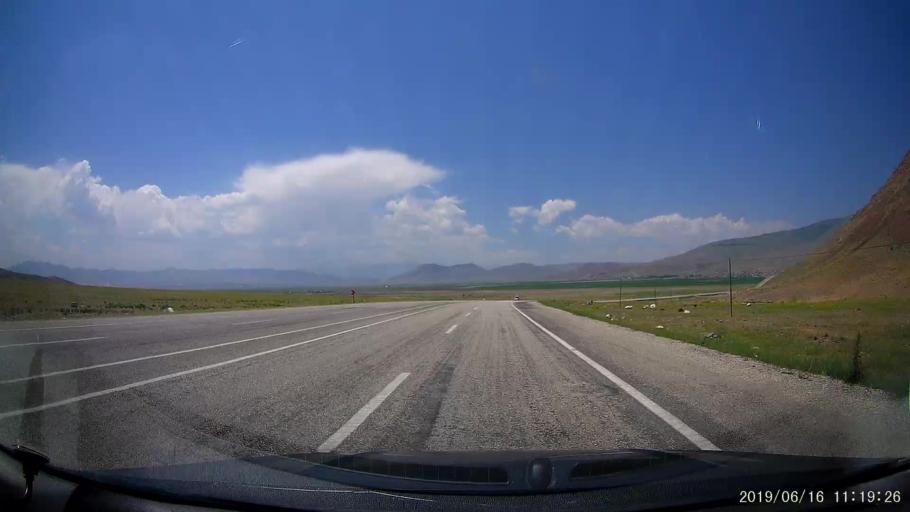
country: TR
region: Agri
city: Dogubayazit
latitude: 39.6985
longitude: 44.1144
